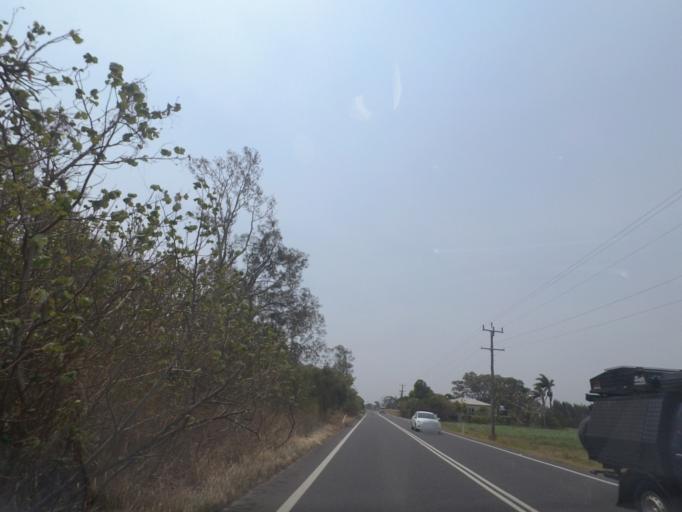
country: AU
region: New South Wales
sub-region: Ballina
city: Ballina
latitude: -28.9706
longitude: 153.4611
